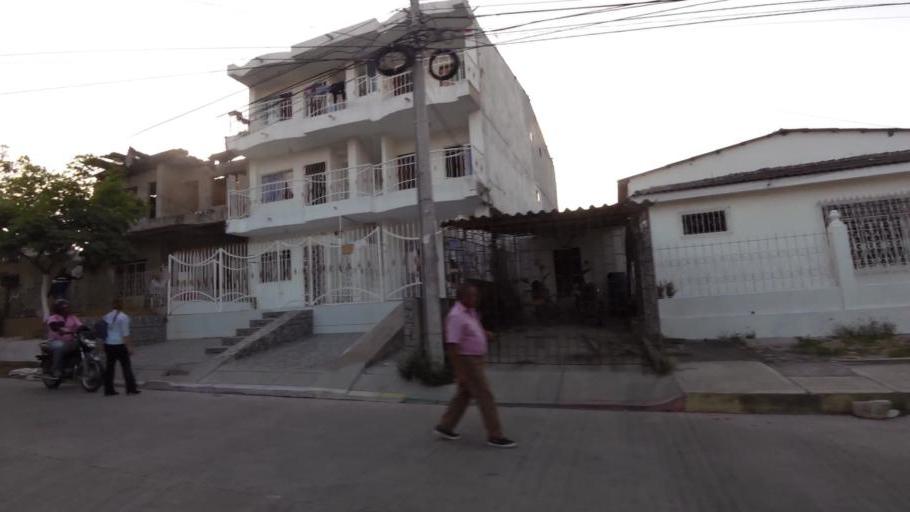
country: CO
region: Bolivar
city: Cartagena
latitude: 10.3886
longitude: -75.4873
